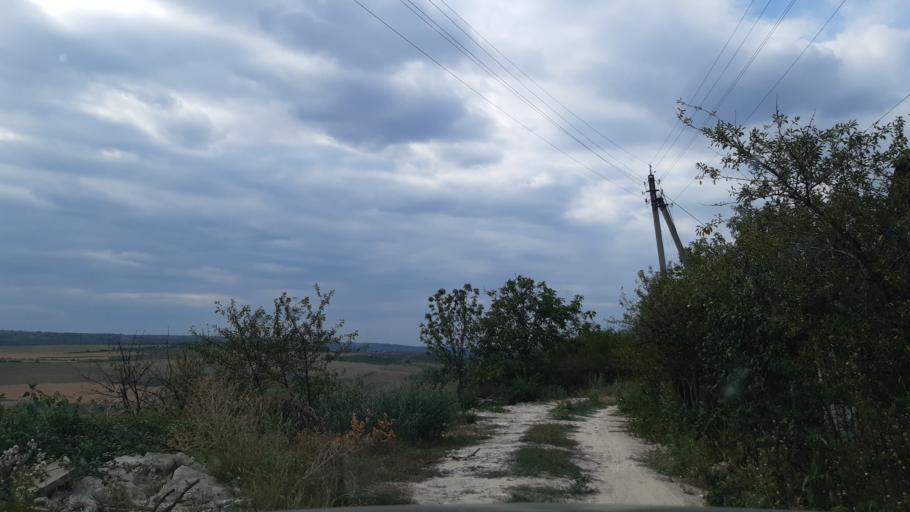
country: MD
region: Chisinau
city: Vatra
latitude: 47.0480
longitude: 28.7315
